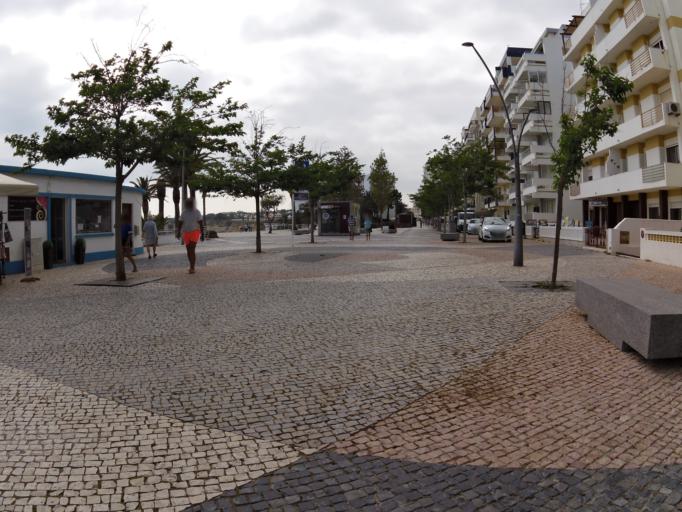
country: PT
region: Faro
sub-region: Silves
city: Armacao de Pera
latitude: 37.1018
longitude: -8.3636
